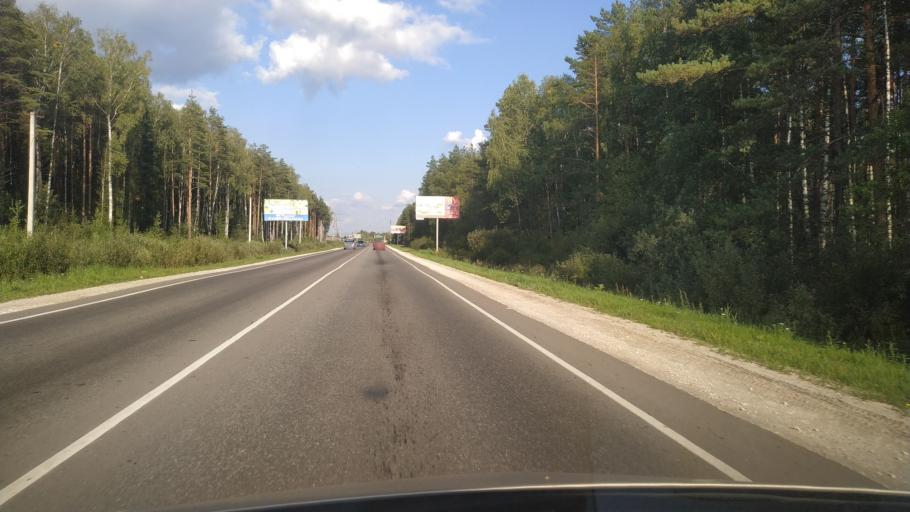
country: RU
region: Moskovskaya
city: Shaturtorf
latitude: 55.5789
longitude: 39.4526
